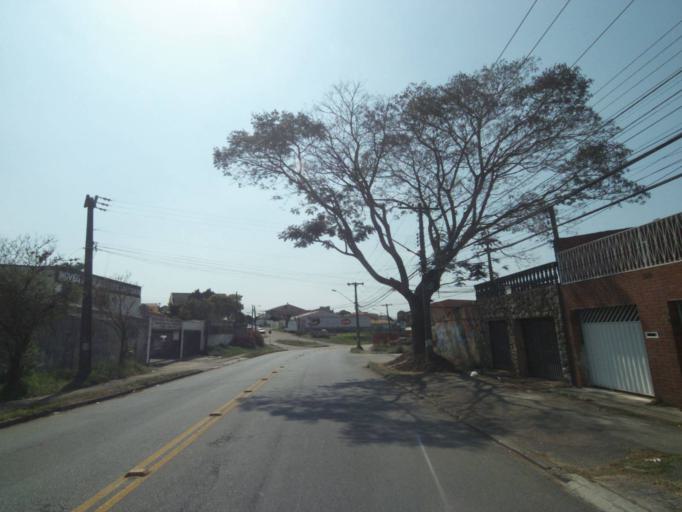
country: BR
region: Parana
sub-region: Curitiba
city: Curitiba
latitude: -25.4895
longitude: -49.3072
